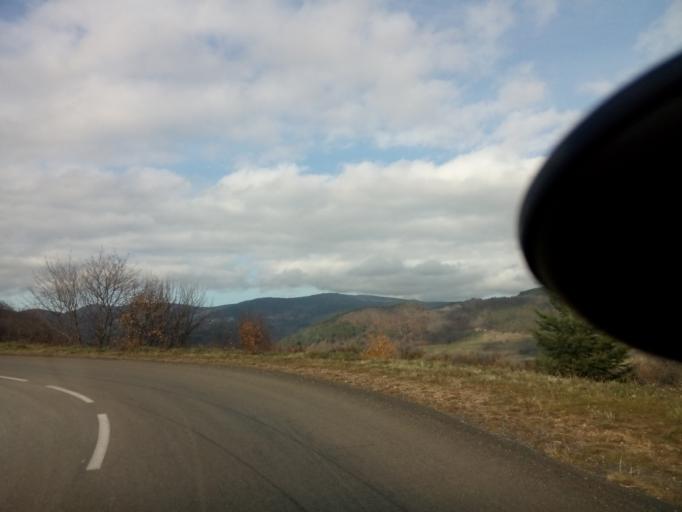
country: FR
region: Rhone-Alpes
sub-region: Departement de la Loire
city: Bourg-Argental
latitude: 45.2876
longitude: 4.5760
